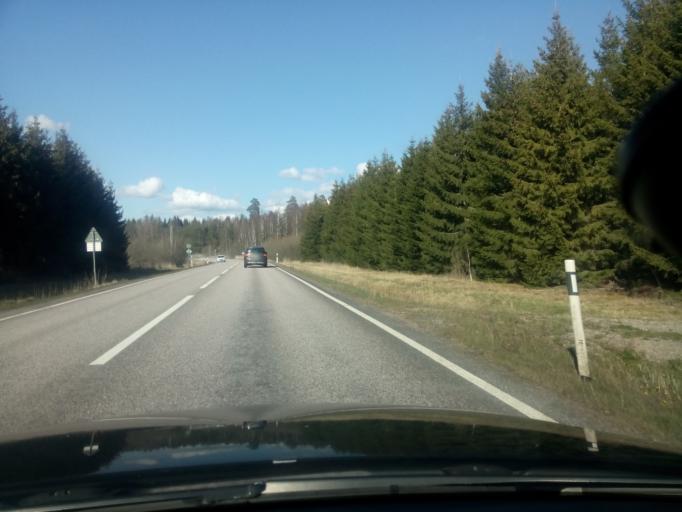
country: SE
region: Soedermanland
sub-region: Strangnas Kommun
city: Akers Styckebruk
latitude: 59.2348
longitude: 16.9352
